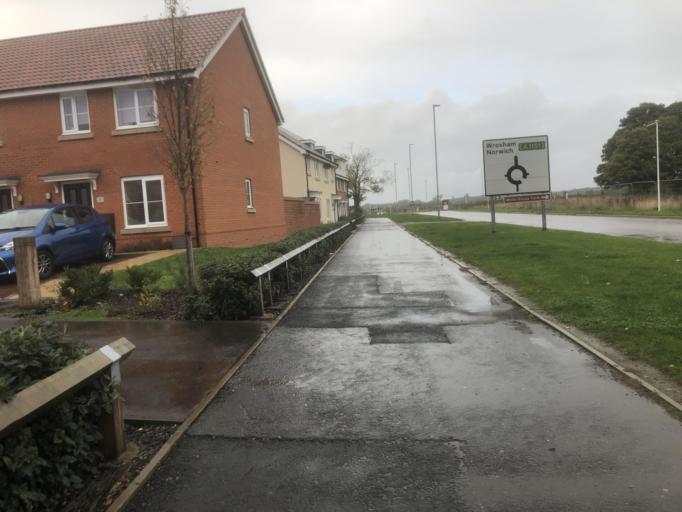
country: GB
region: England
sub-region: Norfolk
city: Spixworth
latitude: 52.6569
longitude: 1.3490
